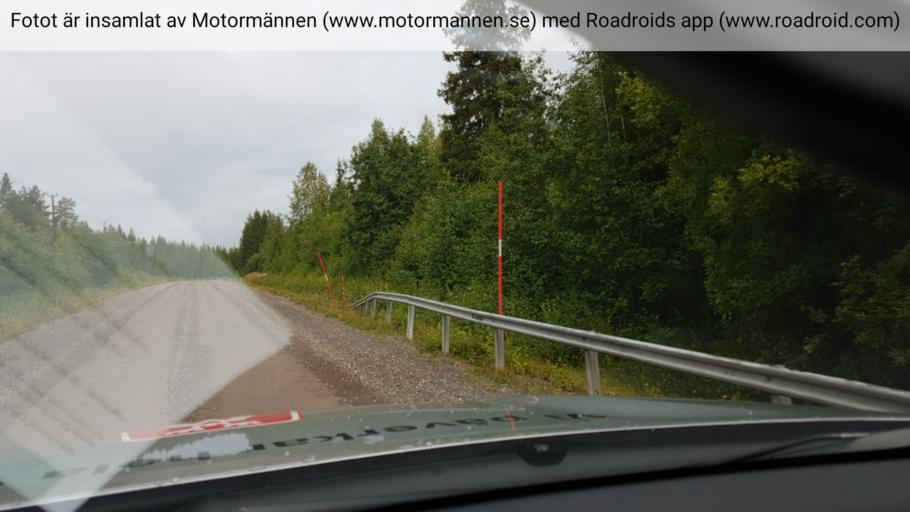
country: SE
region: Norrbotten
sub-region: Alvsbyns Kommun
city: AElvsbyn
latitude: 66.0163
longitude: 21.0413
